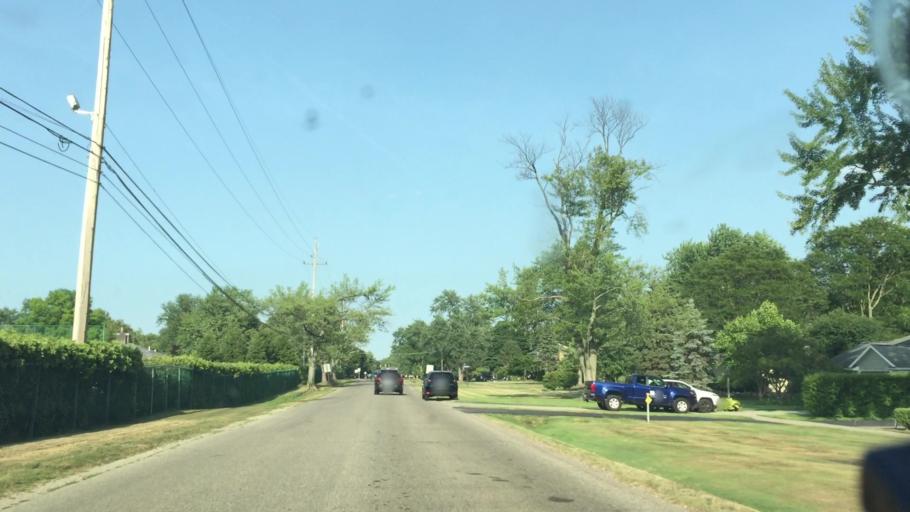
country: US
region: Michigan
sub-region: Oakland County
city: Beverly Hills
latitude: 42.5312
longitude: -83.2316
